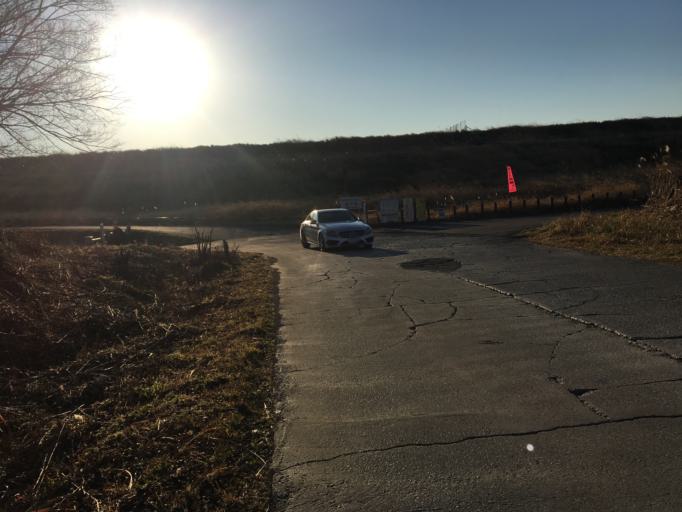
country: JP
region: Saitama
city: Shiki
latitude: 35.8379
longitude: 139.6096
